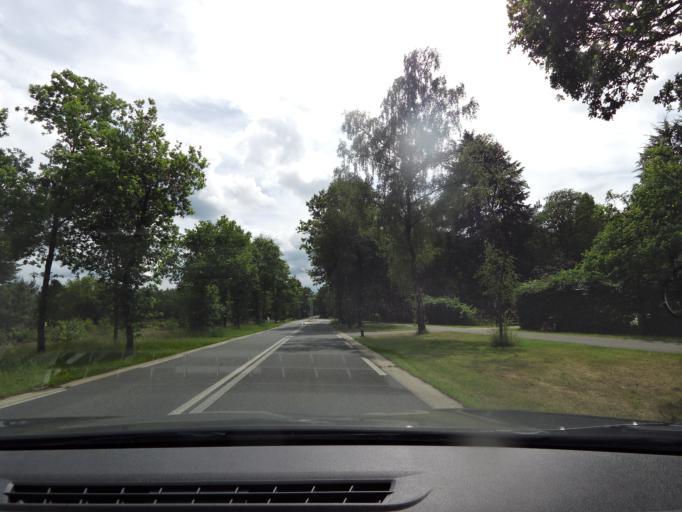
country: NL
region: Gelderland
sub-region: Gemeente Barneveld
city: Garderen
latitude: 52.2210
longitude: 5.7081
